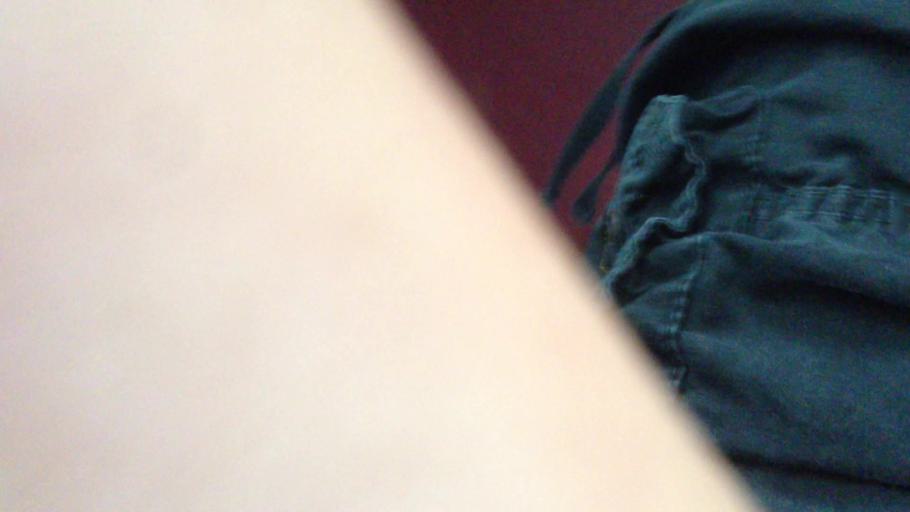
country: US
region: New York
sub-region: Dutchess County
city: Red Hook
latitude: 41.9896
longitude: -73.9155
